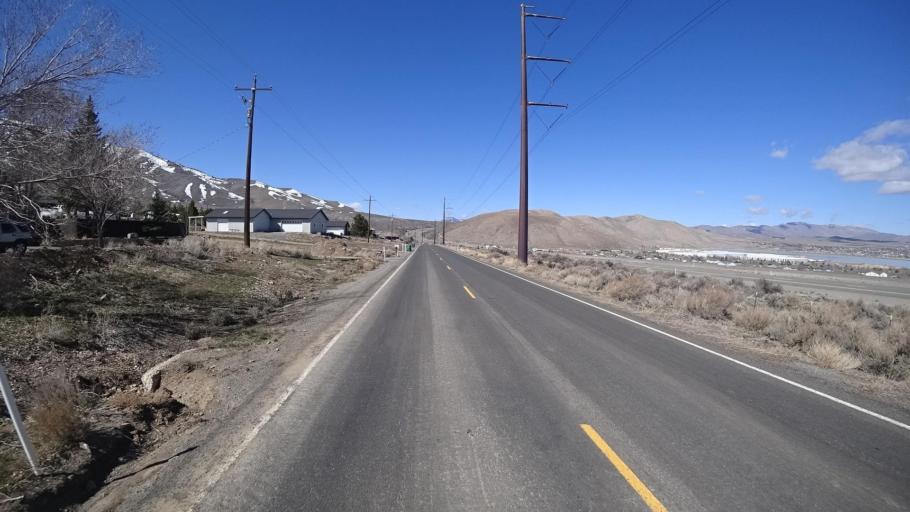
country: US
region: Nevada
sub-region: Washoe County
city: Lemmon Valley
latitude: 39.6255
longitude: -119.9076
